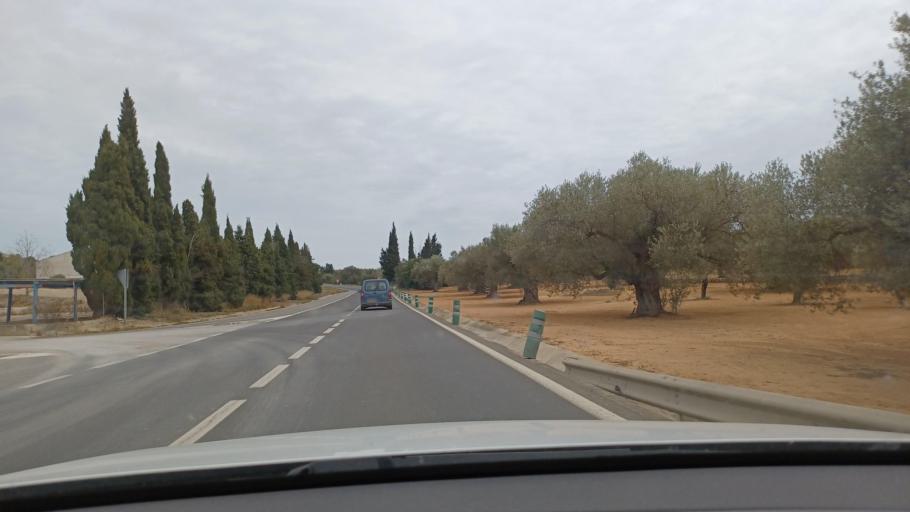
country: ES
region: Catalonia
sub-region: Provincia de Tarragona
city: Masdenverge
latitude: 40.7094
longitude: 0.5401
